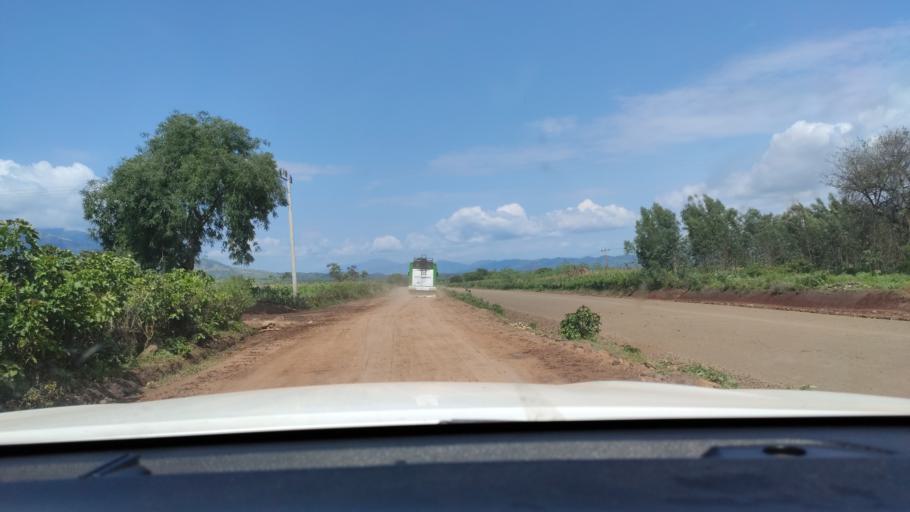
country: ET
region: Southern Nations, Nationalities, and People's Region
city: Felege Neway
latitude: 6.3679
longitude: 36.9936
